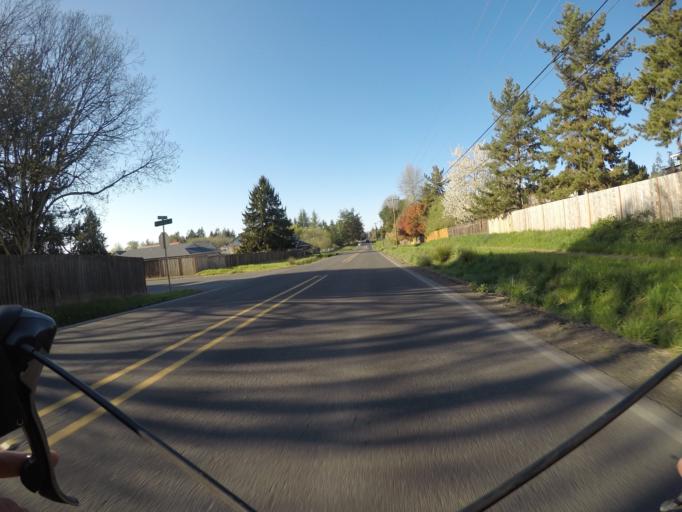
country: US
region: Oregon
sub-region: Washington County
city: Aloha
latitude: 45.4685
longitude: -122.8675
